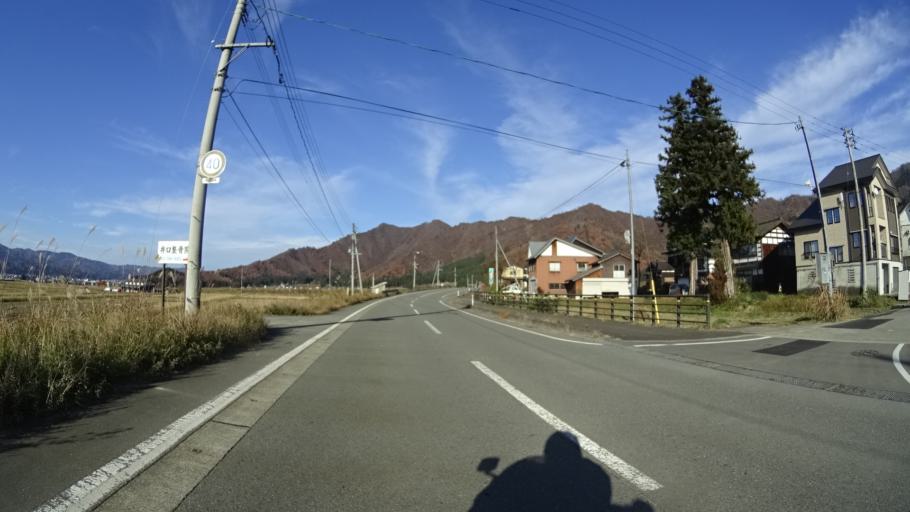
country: JP
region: Niigata
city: Muikamachi
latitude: 37.0339
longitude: 138.8878
